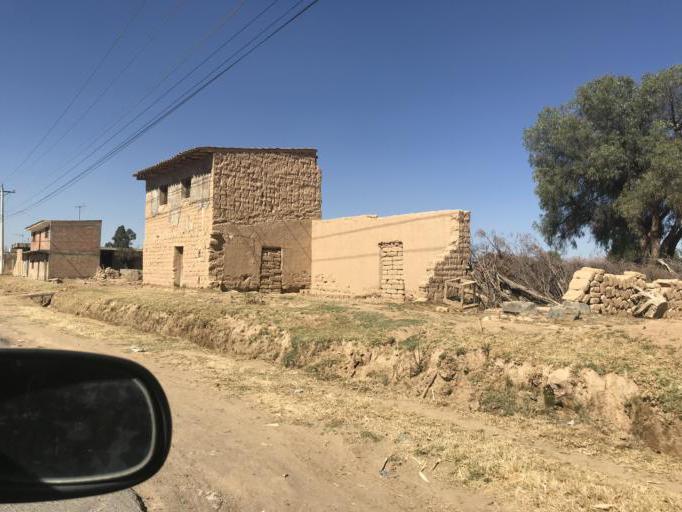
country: BO
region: Cochabamba
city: Cliza
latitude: -17.5965
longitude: -65.9522
